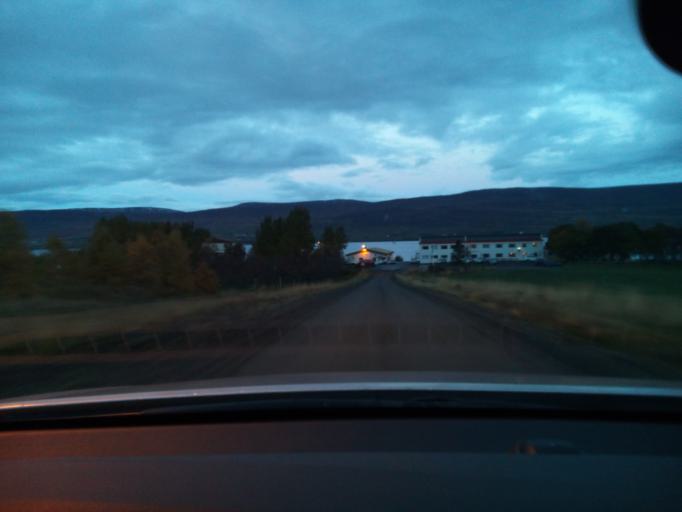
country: IS
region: Northeast
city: Akureyri
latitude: 65.7337
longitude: -18.1677
